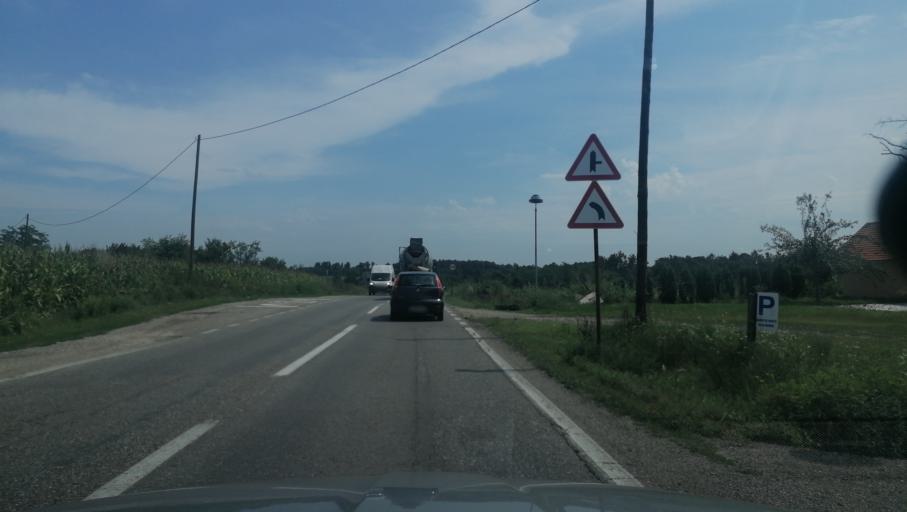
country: BA
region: Republika Srpska
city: Velika Obarska
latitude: 44.7727
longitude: 19.1191
